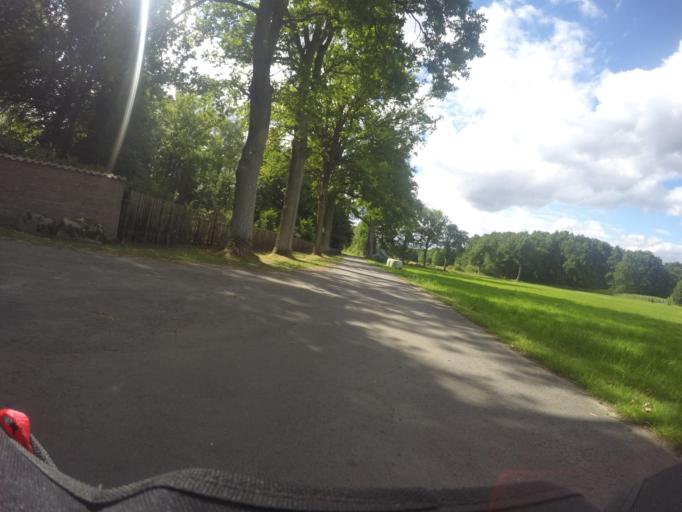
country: DE
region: Lower Saxony
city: Thomasburg
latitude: 53.2205
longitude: 10.6734
